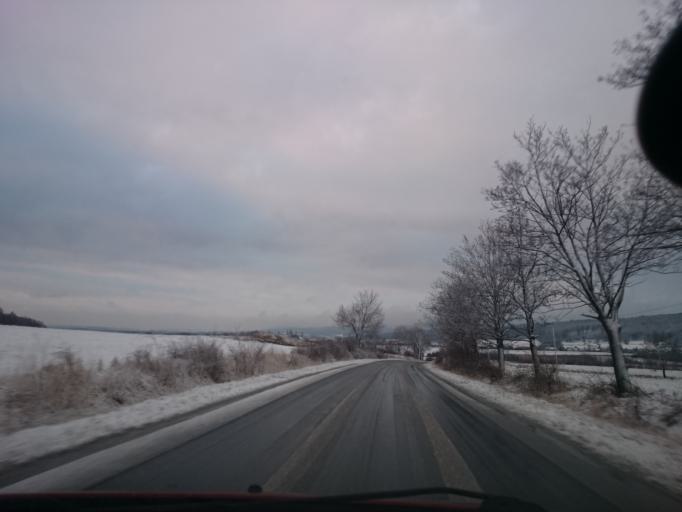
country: PL
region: Lower Silesian Voivodeship
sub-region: Powiat zabkowicki
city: Bardo
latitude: 50.5474
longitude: 16.7201
